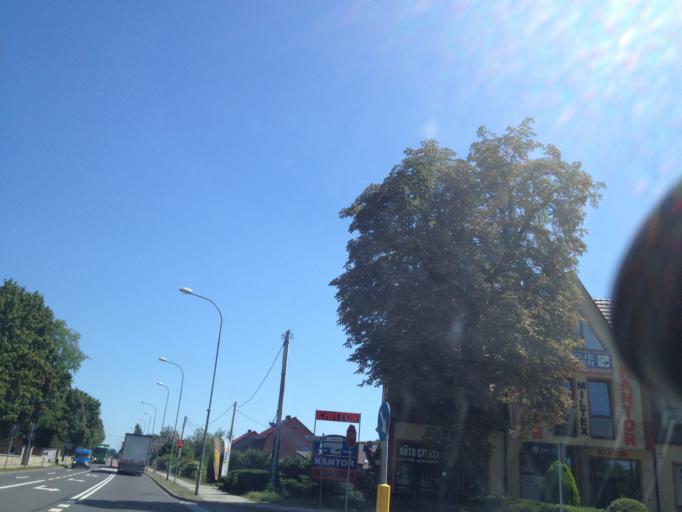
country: PL
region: Lubusz
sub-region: Powiat sulecinski
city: Torzym
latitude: 52.3145
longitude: 15.0586
